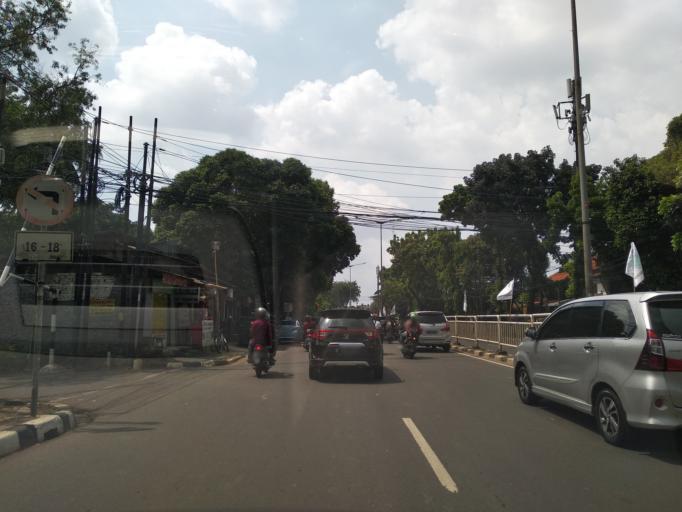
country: ID
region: Jakarta Raya
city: Jakarta
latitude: -6.2415
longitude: 106.8445
